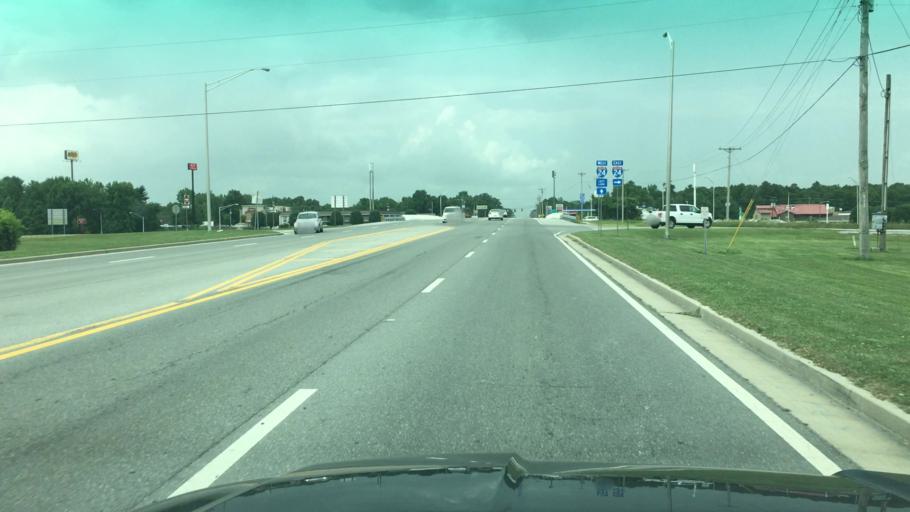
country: US
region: Tennessee
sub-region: Coffee County
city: Manchester
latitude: 35.4980
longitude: -86.0869
